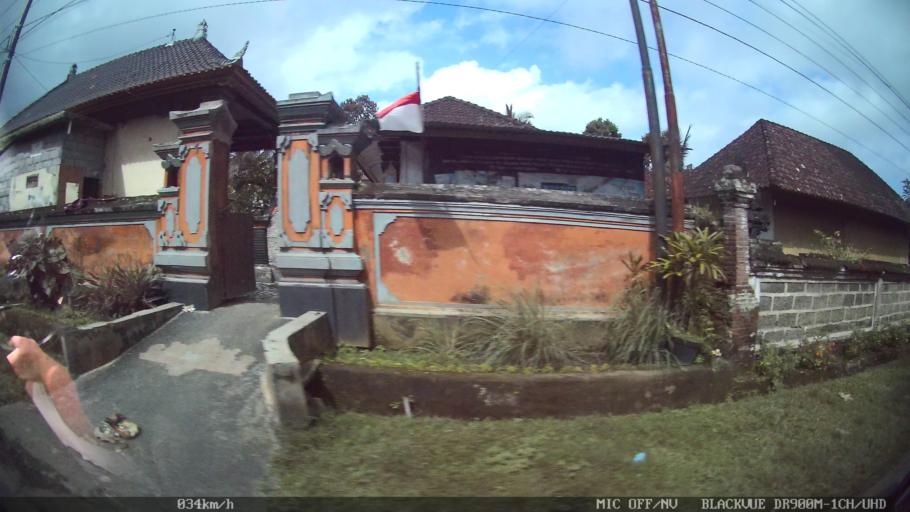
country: ID
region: Bali
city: Banjar Pesalakan
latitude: -8.4838
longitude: 115.3050
